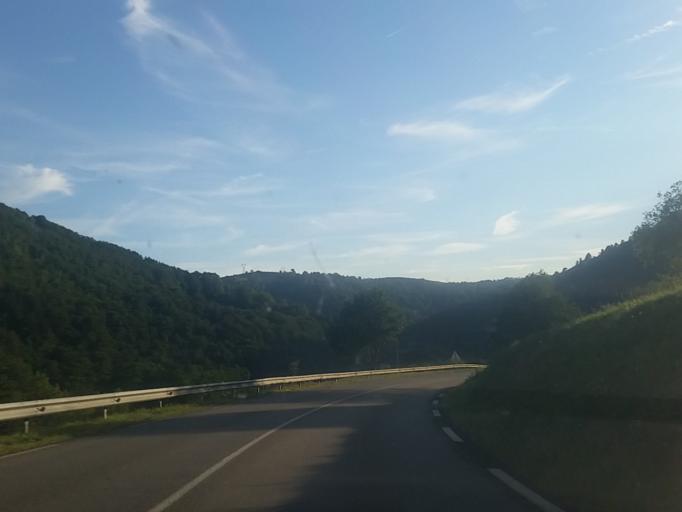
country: FR
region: Auvergne
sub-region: Departement du Cantal
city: Neuveglise
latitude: 44.8939
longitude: 3.0036
